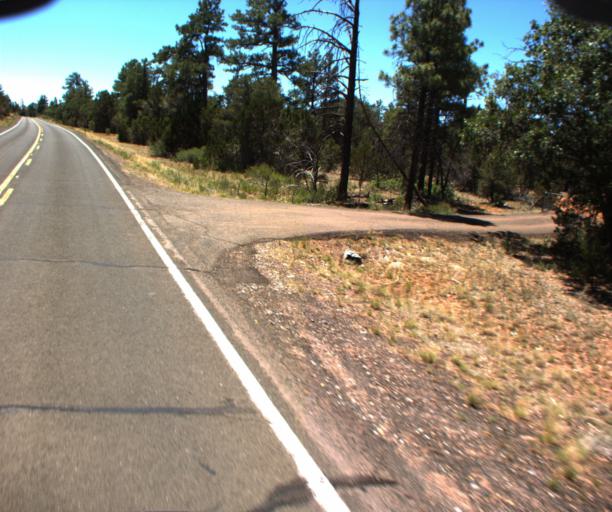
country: US
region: Arizona
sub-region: Gila County
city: Star Valley
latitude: 34.6826
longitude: -111.1128
